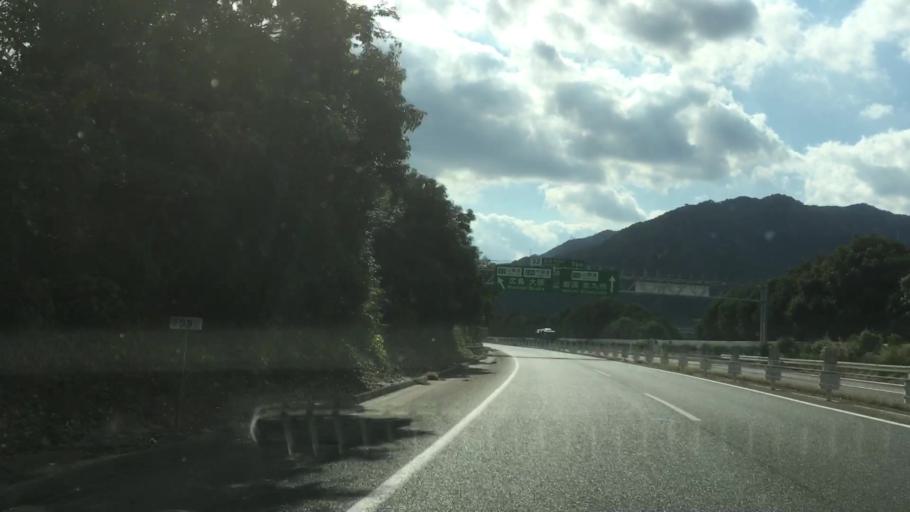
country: JP
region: Hiroshima
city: Hatsukaichi
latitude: 34.3440
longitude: 132.3061
